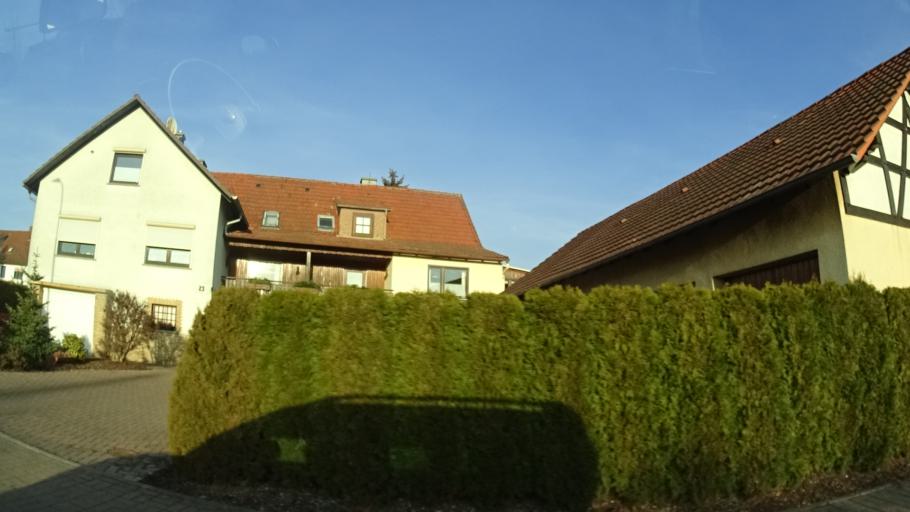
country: DE
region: Bavaria
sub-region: Regierungsbezirk Unterfranken
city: Zeitlofs
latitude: 50.3111
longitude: 9.6273
